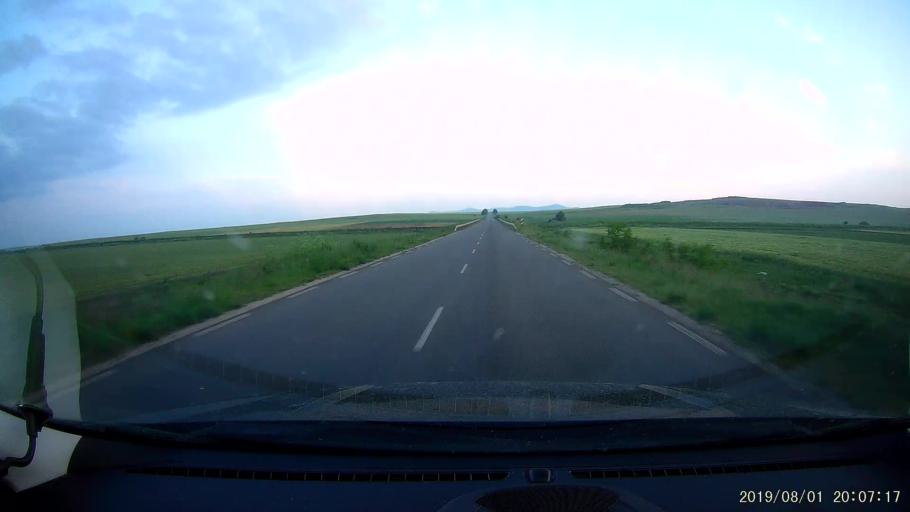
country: BG
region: Yambol
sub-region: Obshtina Yambol
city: Yambol
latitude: 42.5245
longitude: 26.5665
